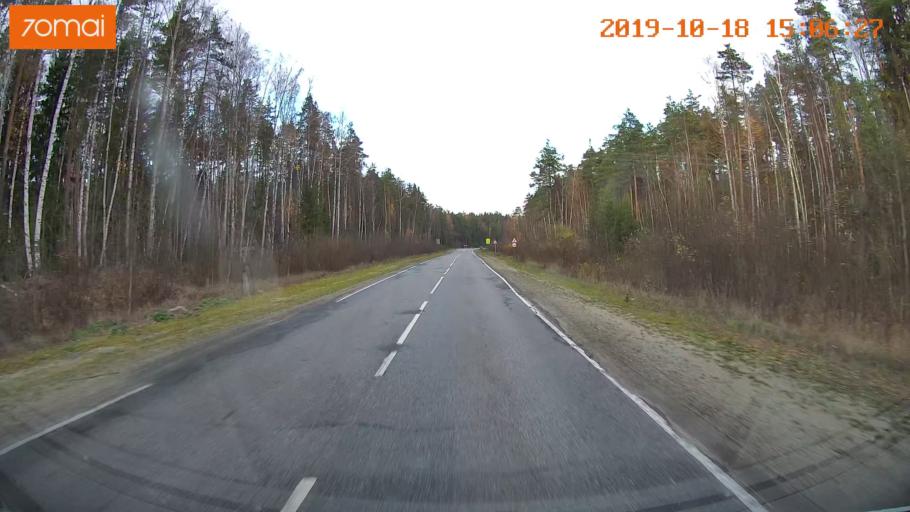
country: RU
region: Vladimir
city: Gus'-Khrustal'nyy
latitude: 55.5303
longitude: 40.5787
